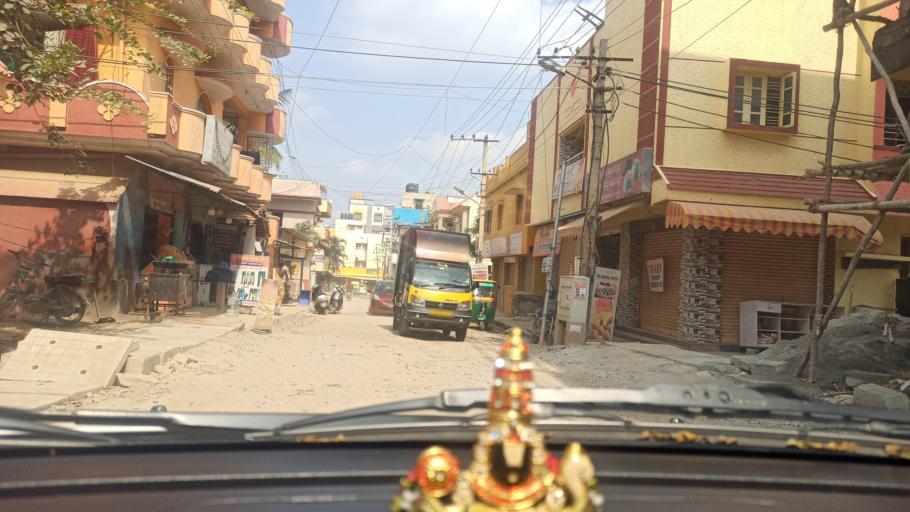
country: IN
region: Karnataka
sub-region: Bangalore Urban
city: Bangalore
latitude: 13.0158
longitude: 77.6654
